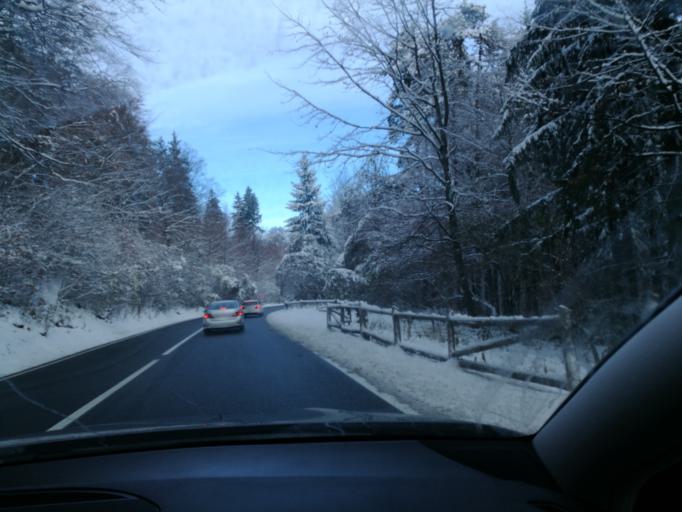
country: RO
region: Brasov
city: Brasov
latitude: 45.6279
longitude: 25.5502
